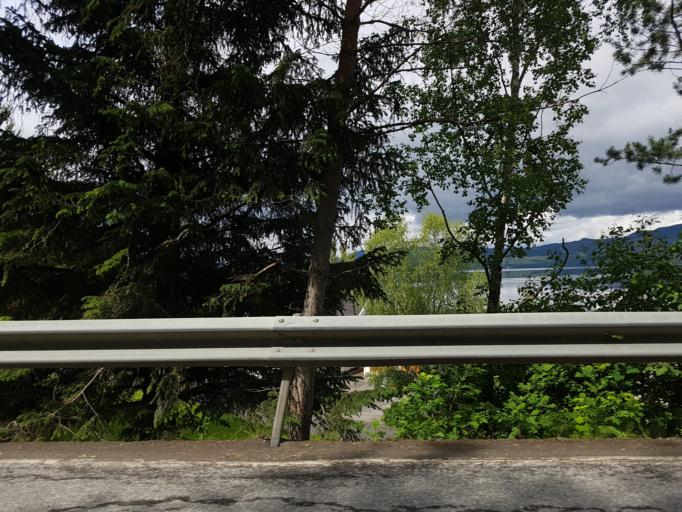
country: NO
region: Sor-Trondelag
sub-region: Selbu
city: Mebonden
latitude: 63.2338
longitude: 11.0386
